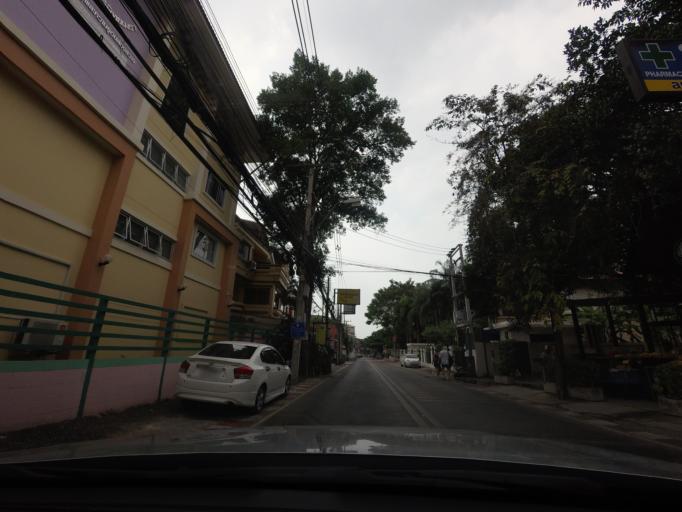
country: TH
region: Chon Buri
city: Phatthaya
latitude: 12.9642
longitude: 100.8885
